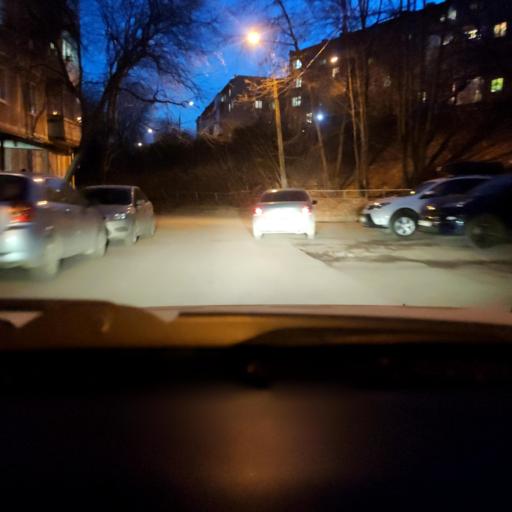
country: RU
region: Perm
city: Perm
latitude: 57.9825
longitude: 56.2242
